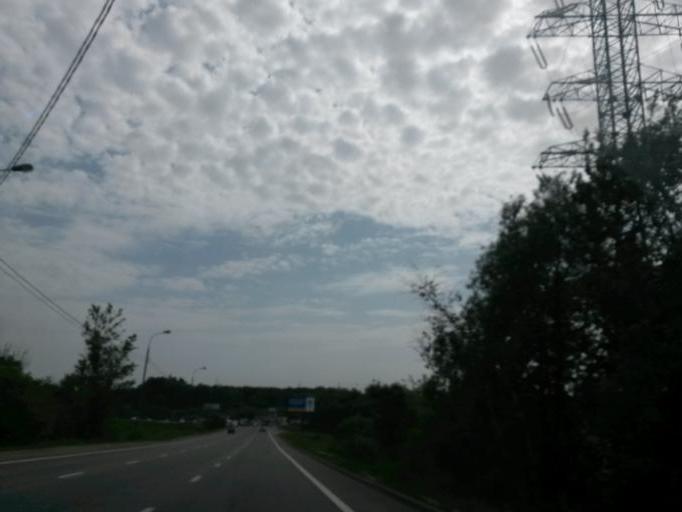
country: RU
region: Moscow
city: Annino
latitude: 55.5705
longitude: 37.5974
